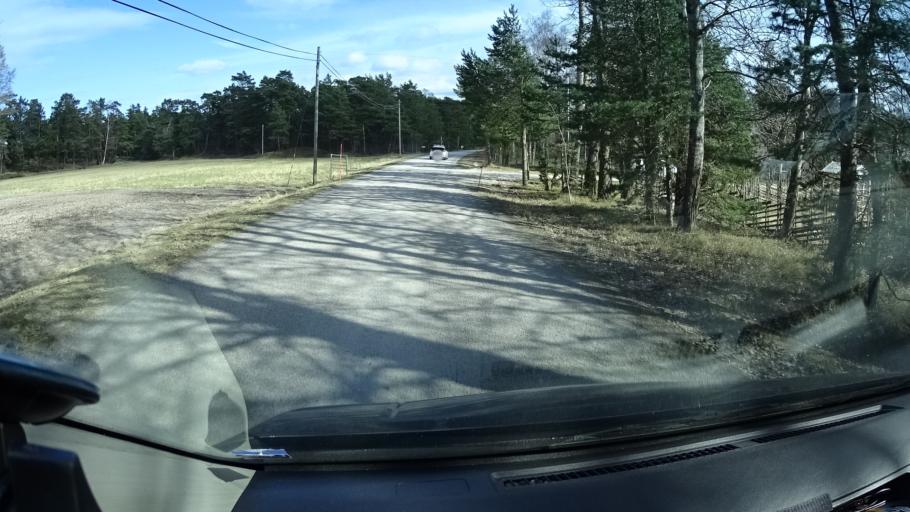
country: SE
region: Gotland
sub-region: Gotland
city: Slite
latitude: 57.9569
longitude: 19.2600
